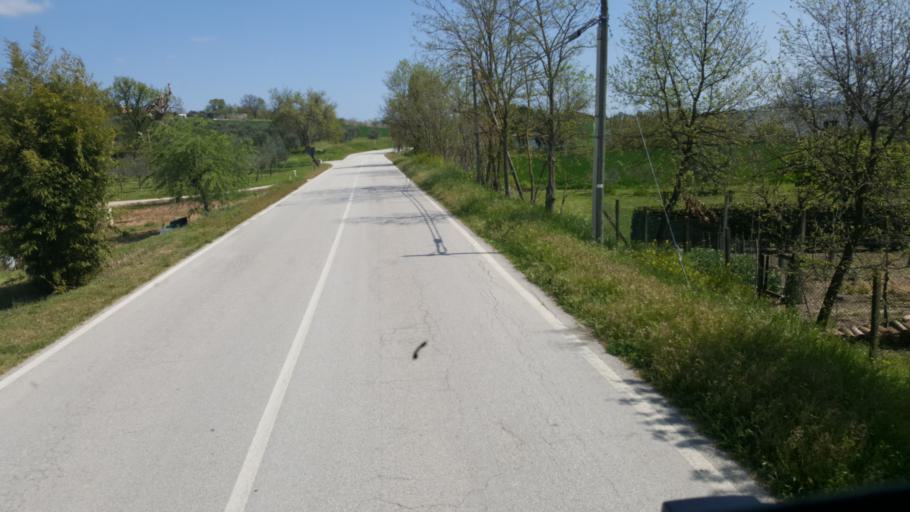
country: IT
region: The Marches
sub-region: Provincia di Macerata
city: Montecassiano
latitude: 43.3542
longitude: 13.4502
